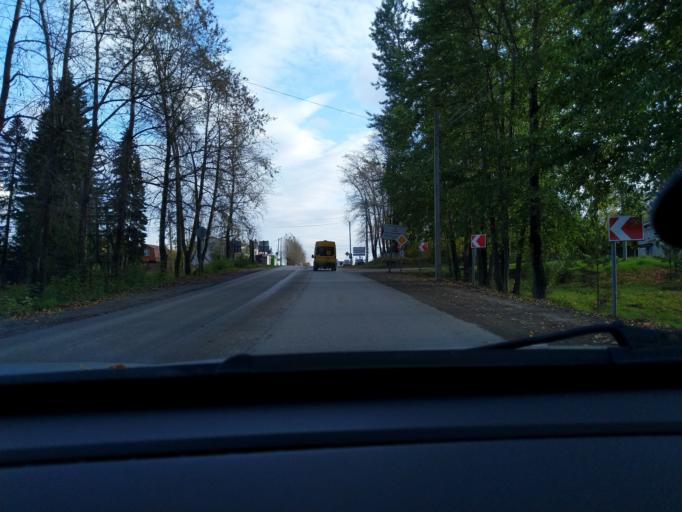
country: RU
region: Perm
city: Polazna
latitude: 58.2856
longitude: 56.4100
